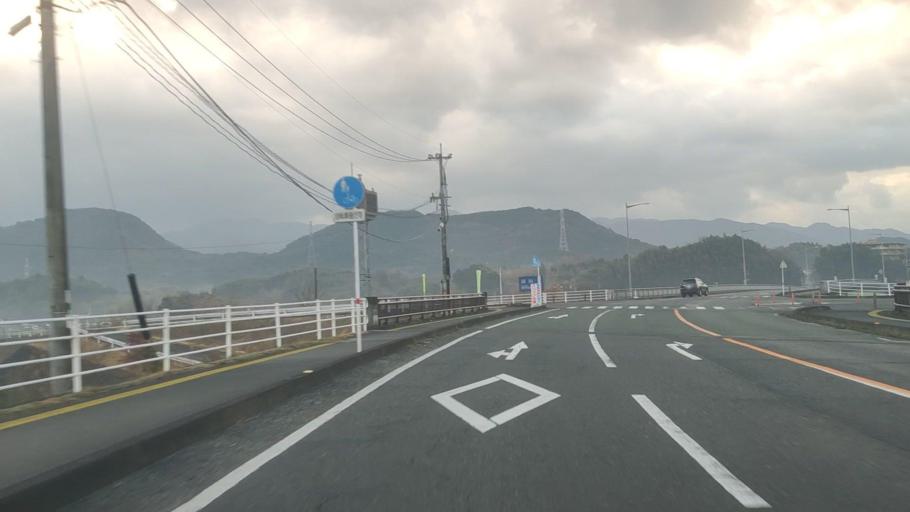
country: JP
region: Kumamoto
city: Matsubase
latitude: 32.6435
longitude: 130.8128
